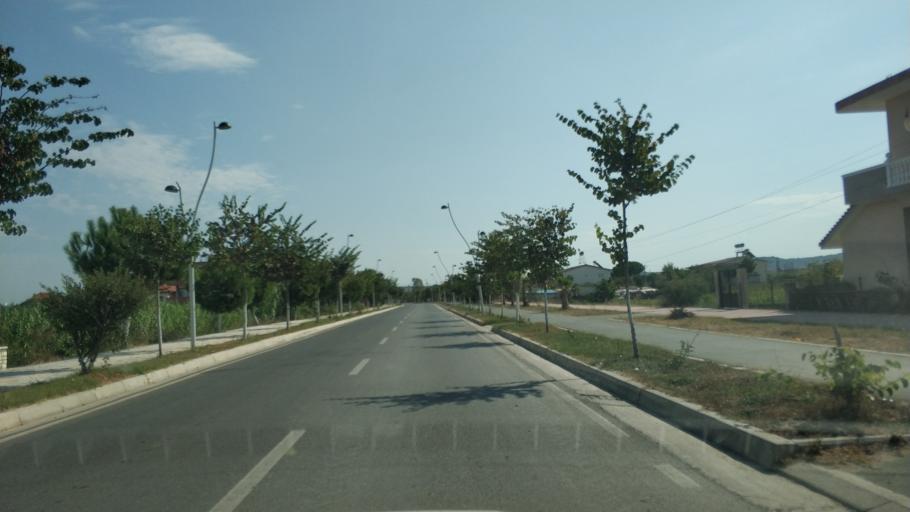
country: AL
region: Fier
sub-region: Rrethi i Lushnjes
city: Divjake
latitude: 40.9924
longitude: 19.5182
